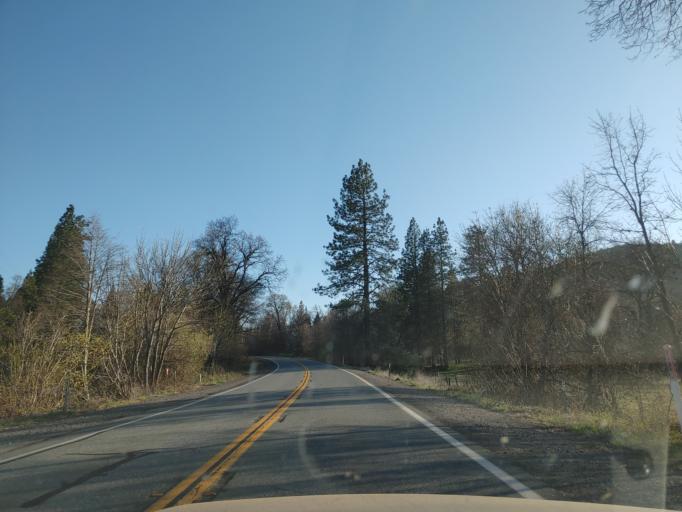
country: US
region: California
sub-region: Shasta County
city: Burney
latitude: 40.8151
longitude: -121.9379
